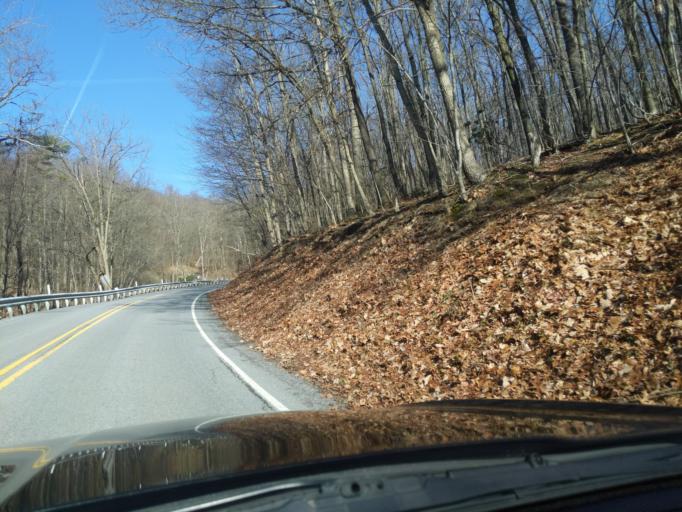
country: US
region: Pennsylvania
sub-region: Blair County
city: Tipton
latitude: 40.6221
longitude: -78.2748
